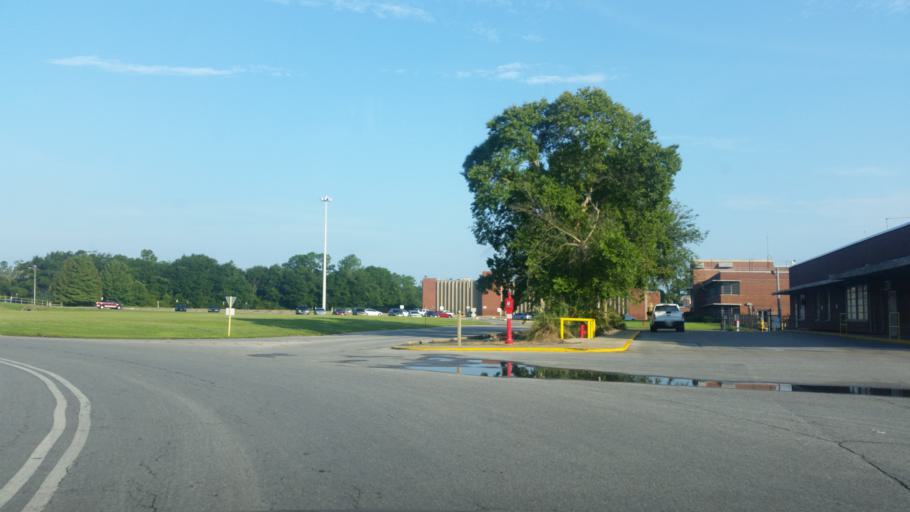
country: US
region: Florida
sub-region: Escambia County
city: Gonzalez
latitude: 30.5948
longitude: -87.2557
